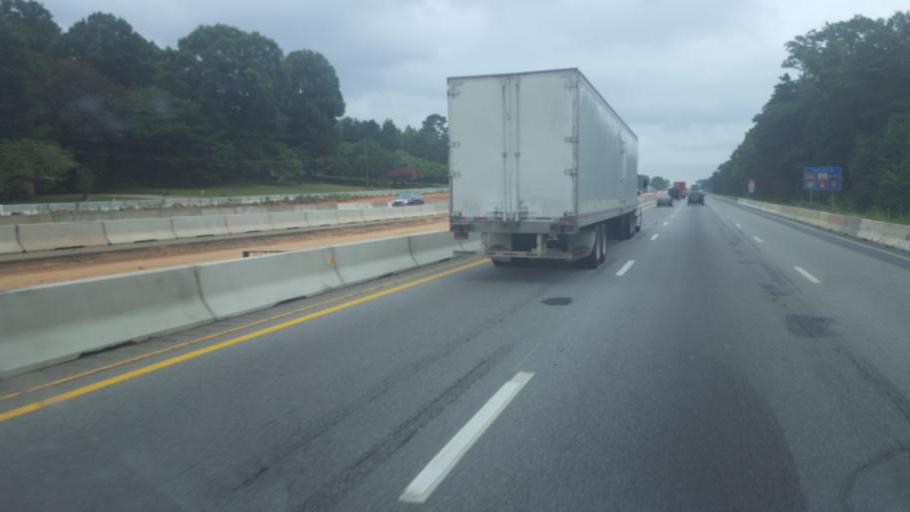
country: US
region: North Carolina
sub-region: Gaston County
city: Davidson
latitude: 35.5391
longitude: -80.8603
